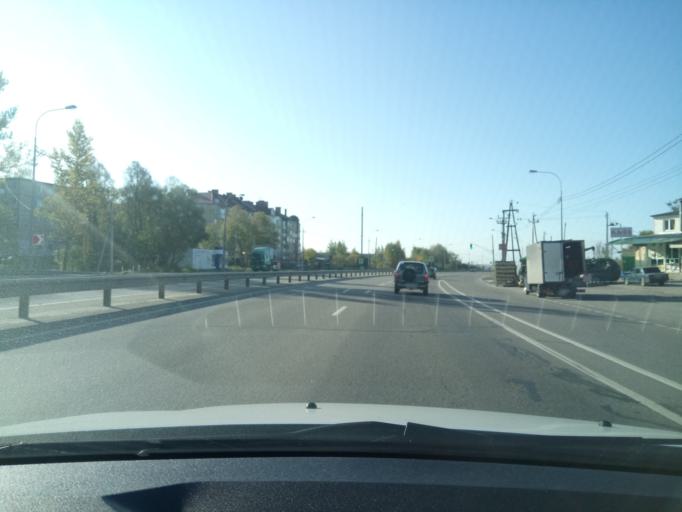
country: RU
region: Nizjnij Novgorod
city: Burevestnik
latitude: 56.1643
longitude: 43.9161
